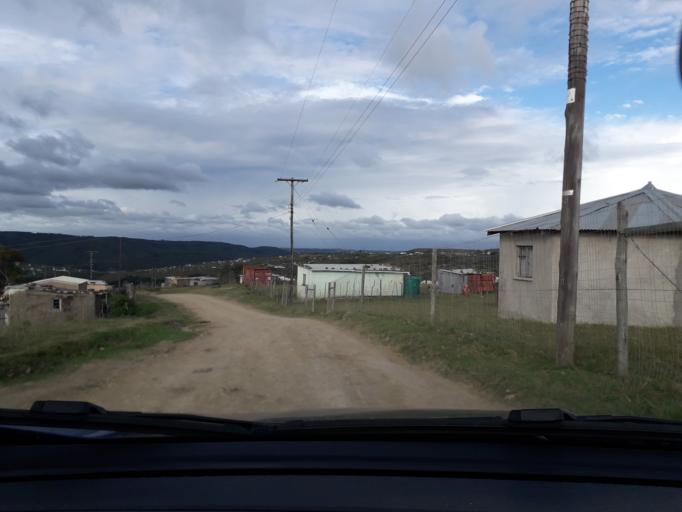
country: ZA
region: Eastern Cape
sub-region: Buffalo City Metropolitan Municipality
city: East London
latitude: -32.8059
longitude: 27.9570
